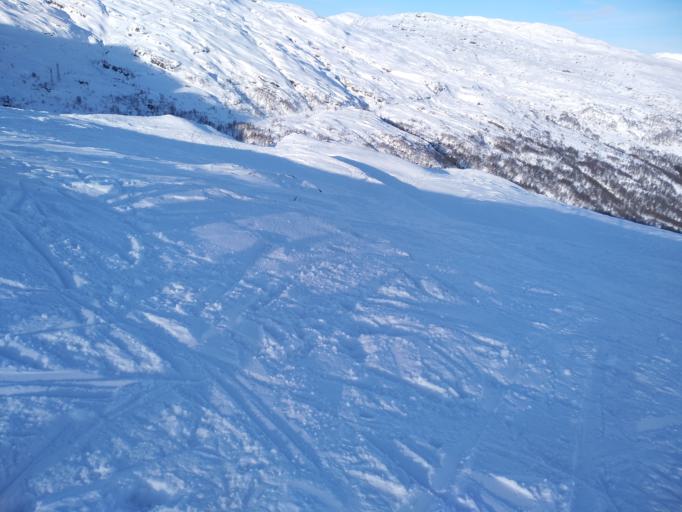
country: NO
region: Rogaland
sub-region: Suldal
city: Sand
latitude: 59.6142
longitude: 6.2246
